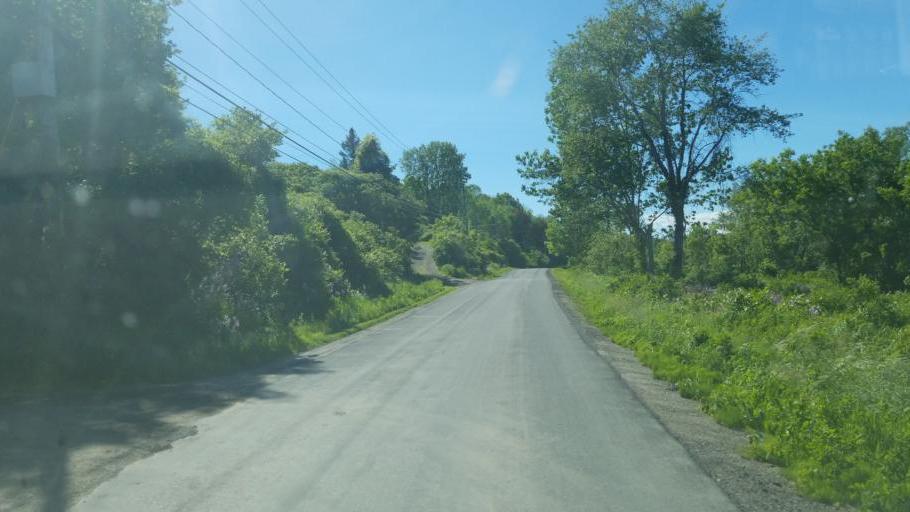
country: US
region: New York
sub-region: Montgomery County
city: Canajoharie
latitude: 42.9054
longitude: -74.5878
